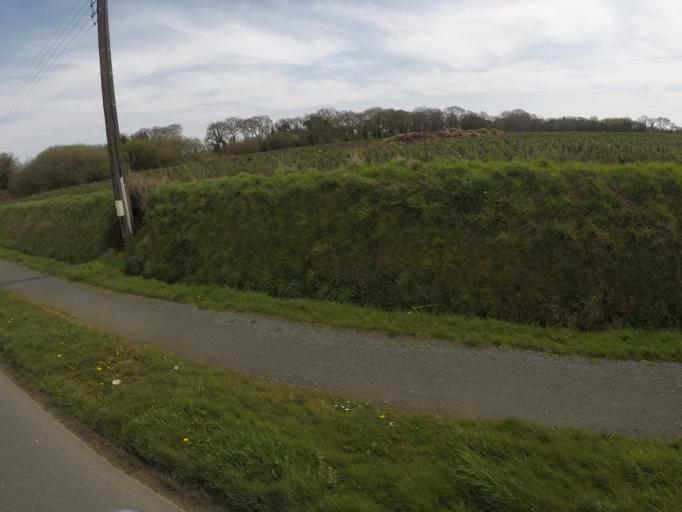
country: FR
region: Brittany
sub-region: Departement des Cotes-d'Armor
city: Plelo
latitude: 48.5498
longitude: -2.9576
